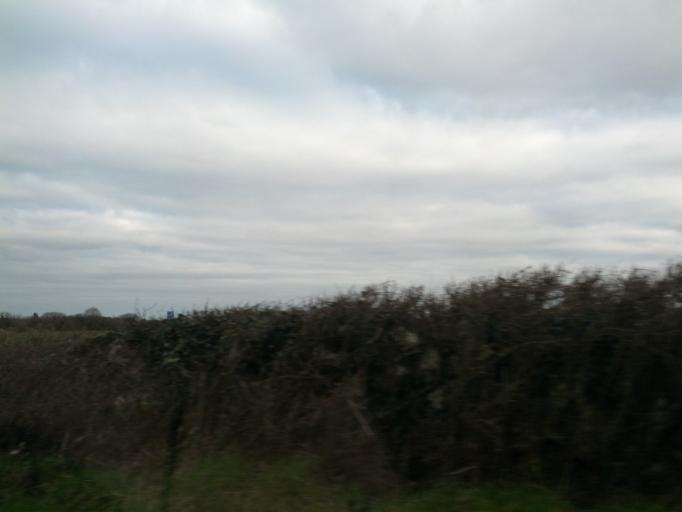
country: IE
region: Connaught
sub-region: County Galway
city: Gort
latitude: 53.1703
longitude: -8.8501
